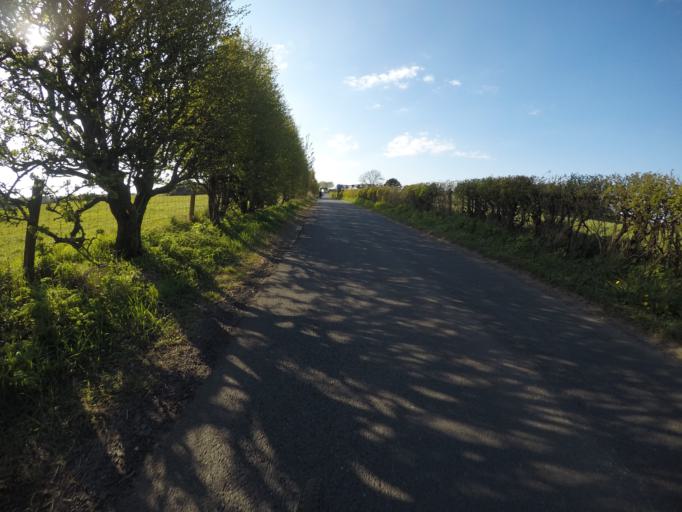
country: GB
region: Scotland
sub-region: North Ayrshire
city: Stevenston
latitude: 55.6493
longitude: -4.7309
